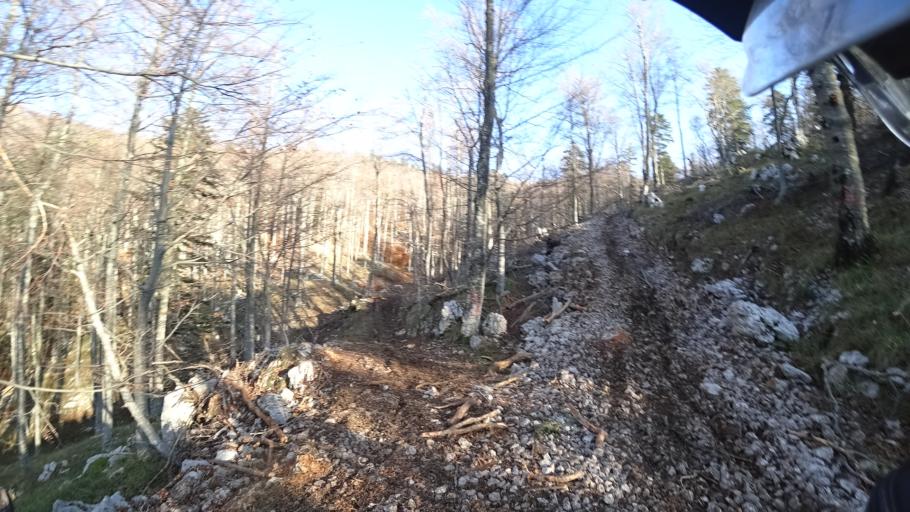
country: HR
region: Primorsko-Goranska
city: Klana
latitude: 45.4792
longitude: 14.4403
